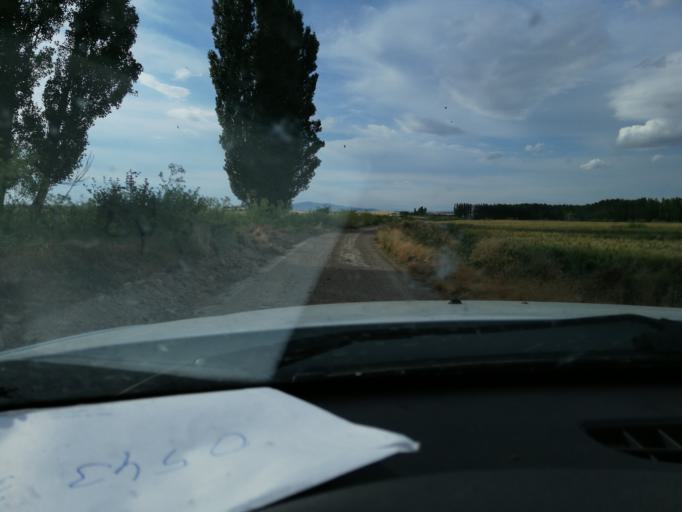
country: TR
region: Kirsehir
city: Kirsehir
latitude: 38.9977
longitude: 34.1250
